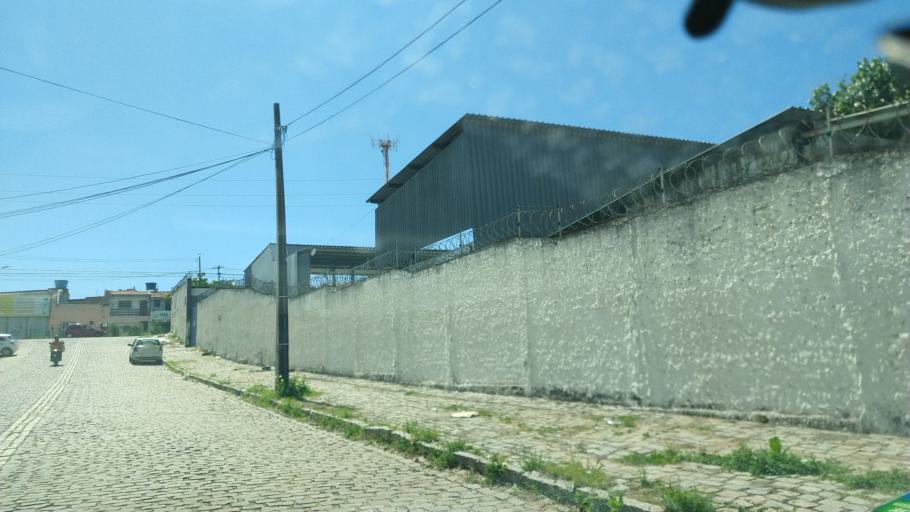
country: BR
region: Rio Grande do Norte
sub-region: Natal
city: Natal
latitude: -5.8107
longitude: -35.2131
